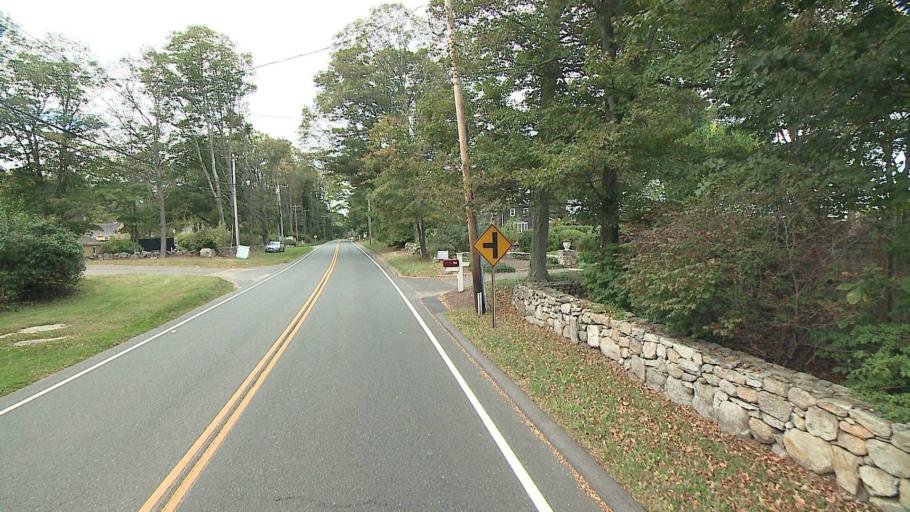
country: US
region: Connecticut
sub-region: Fairfield County
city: Wilton
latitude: 41.2211
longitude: -73.4759
